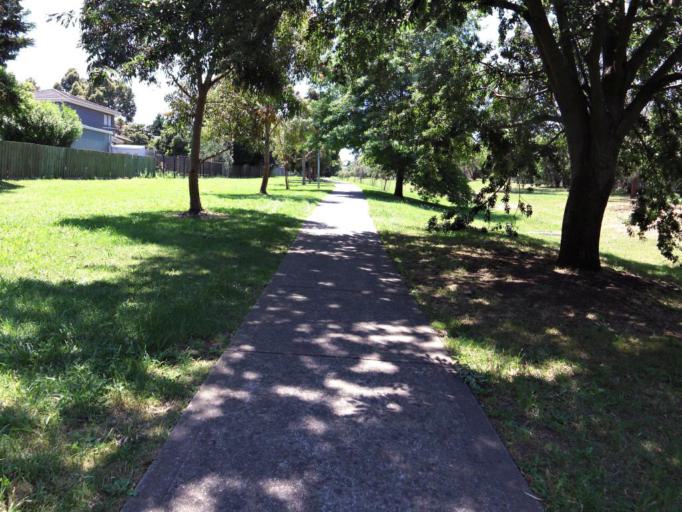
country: AU
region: Victoria
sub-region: Casey
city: Endeavour Hills
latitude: -37.9862
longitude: 145.2605
